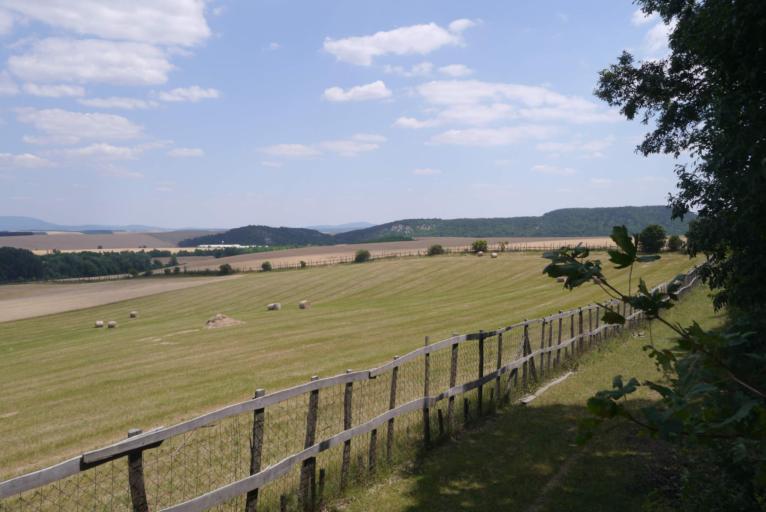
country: HU
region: Komarom-Esztergom
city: Bajna
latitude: 47.5967
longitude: 18.5896
